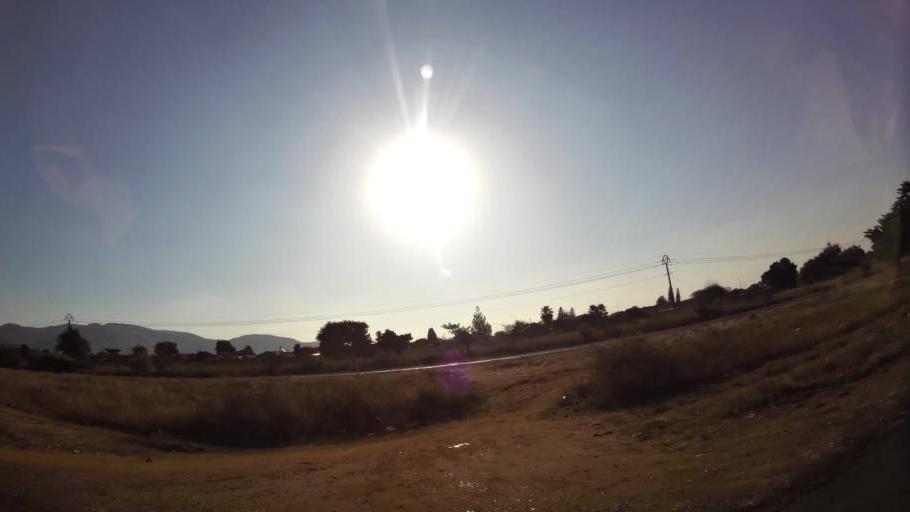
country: ZA
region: North-West
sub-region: Bojanala Platinum District Municipality
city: Rustenburg
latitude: -25.6500
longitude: 27.2238
